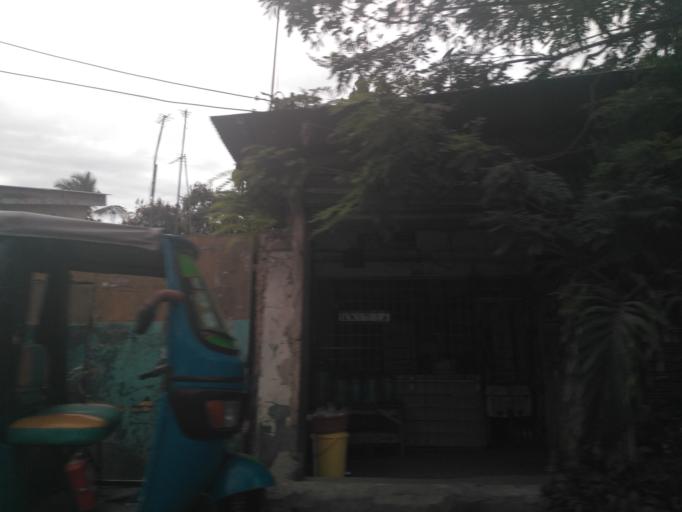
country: TZ
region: Dar es Salaam
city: Magomeni
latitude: -6.7965
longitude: 39.2659
